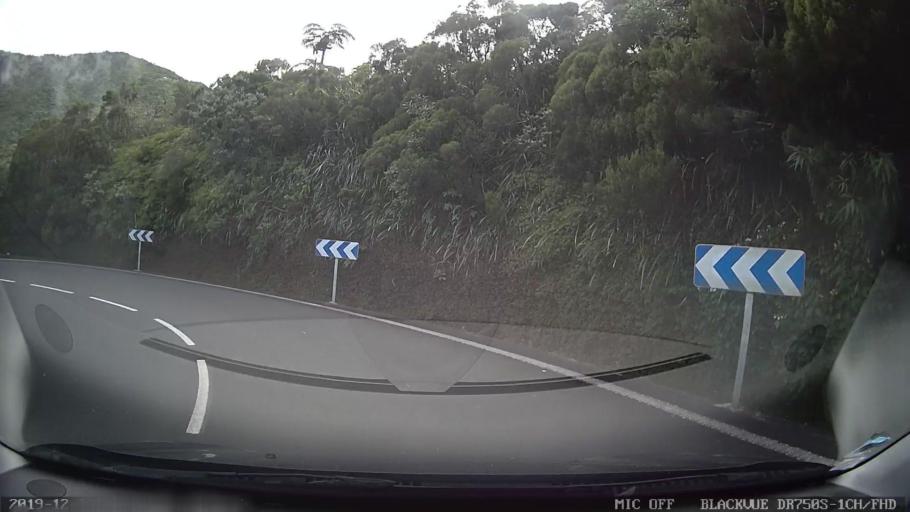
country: RE
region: Reunion
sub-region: Reunion
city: Cilaos
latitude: -21.1574
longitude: 55.5976
